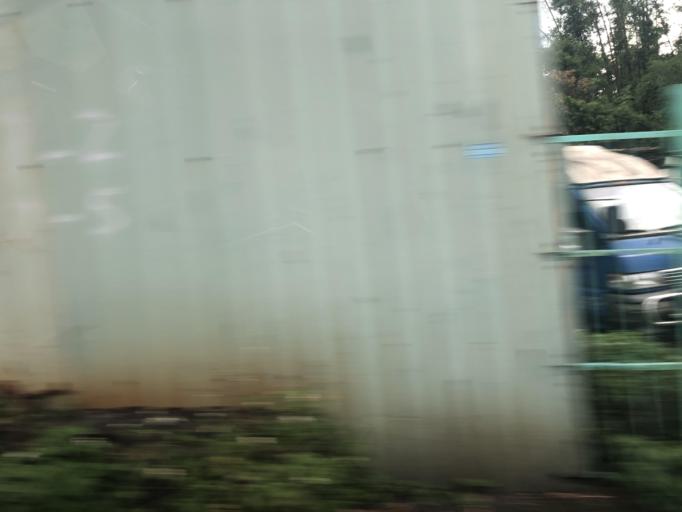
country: TW
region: Taiwan
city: Daxi
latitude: 24.9203
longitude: 121.3584
